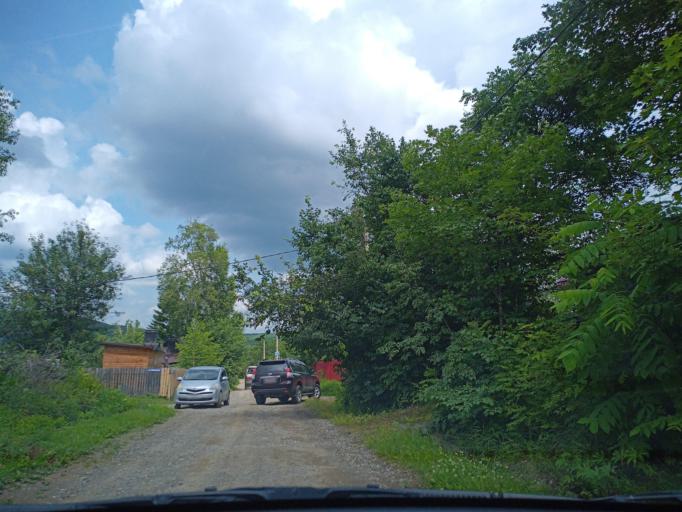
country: RU
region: Khabarovsk Krai
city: Korfovskiy
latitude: 48.3217
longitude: 135.1004
